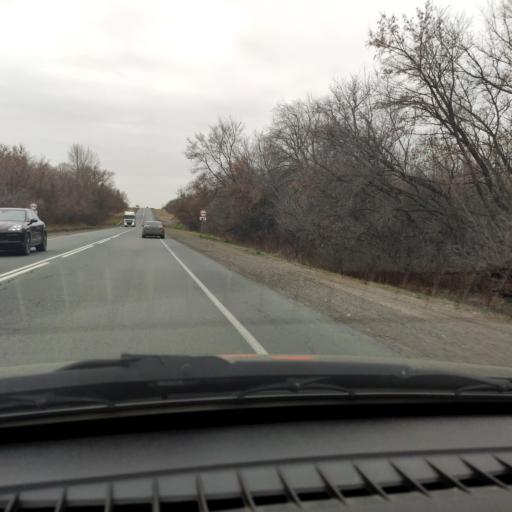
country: RU
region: Samara
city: Zhigulevsk
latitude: 53.3545
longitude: 49.4548
